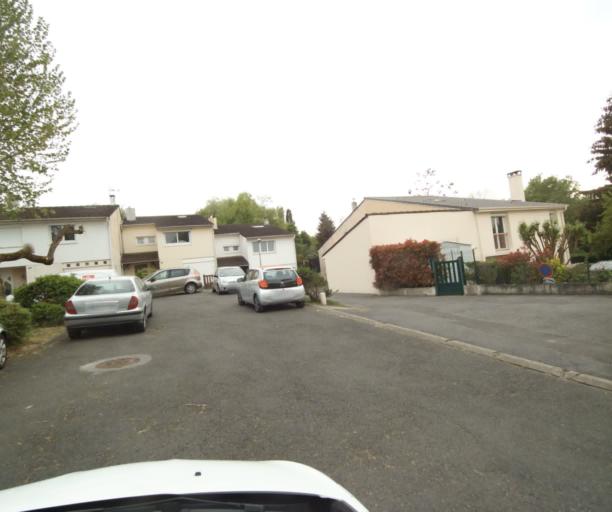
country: FR
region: Ile-de-France
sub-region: Departement de Seine-et-Marne
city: Torcy
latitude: 48.8574
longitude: 2.6596
